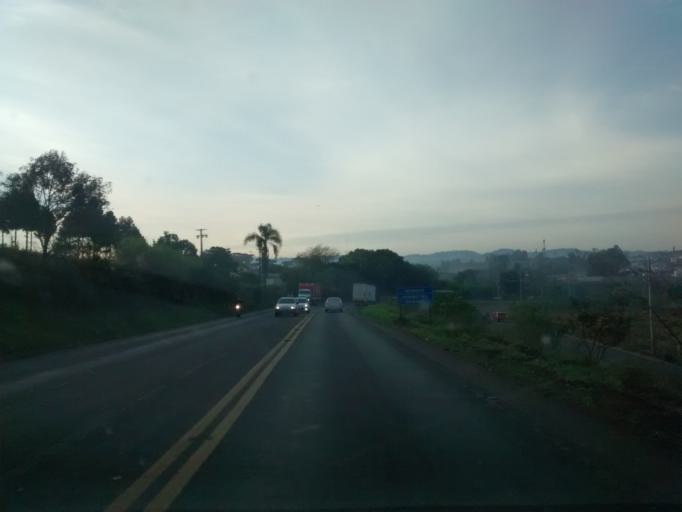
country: BR
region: Parana
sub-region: Francisco Beltrao
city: Francisco Beltrao
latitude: -26.1366
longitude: -53.0342
